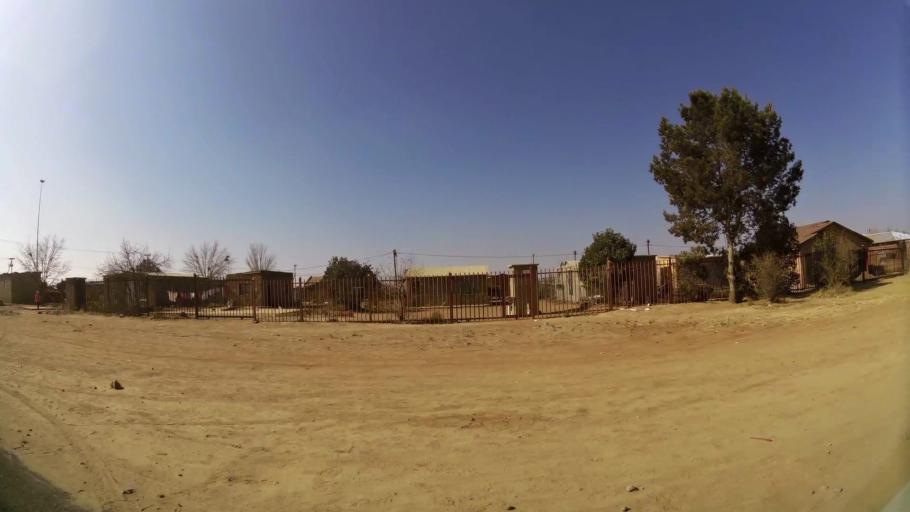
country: ZA
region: Orange Free State
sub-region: Mangaung Metropolitan Municipality
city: Bloemfontein
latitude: -29.1905
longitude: 26.2833
